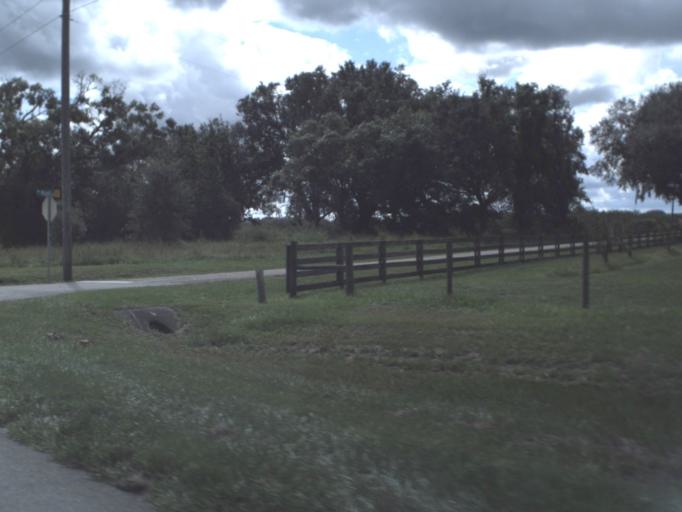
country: US
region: Florida
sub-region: DeSoto County
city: Arcadia
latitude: 27.2637
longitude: -81.9881
